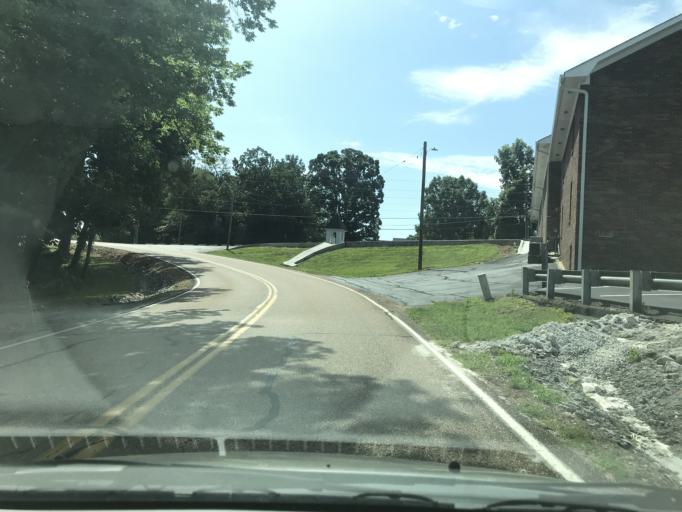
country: US
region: Tennessee
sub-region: Hamilton County
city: Lakesite
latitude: 35.1668
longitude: -85.0590
